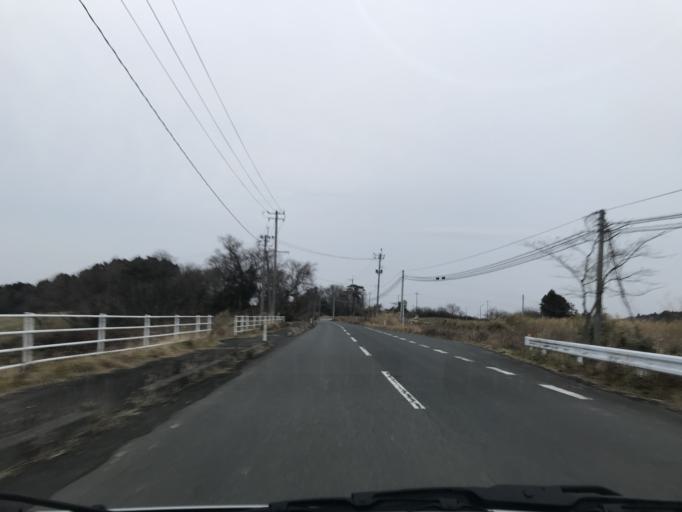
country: JP
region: Miyagi
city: Kogota
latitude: 38.6959
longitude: 141.0953
